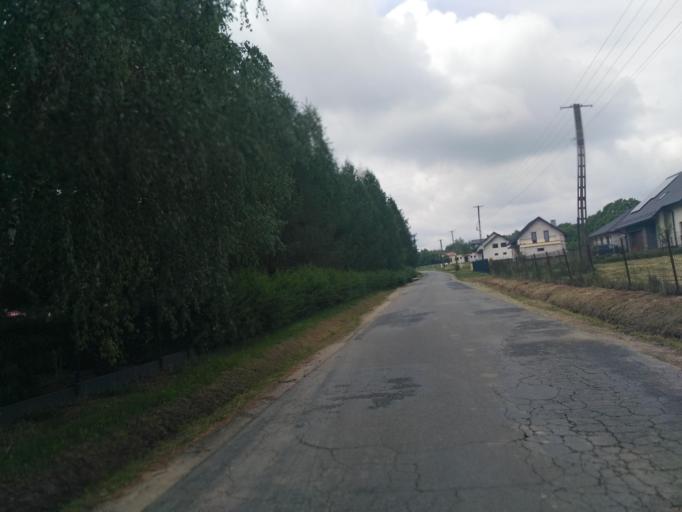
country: PL
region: Subcarpathian Voivodeship
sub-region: Powiat krosnienski
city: Chorkowka
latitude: 49.6714
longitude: 21.6589
